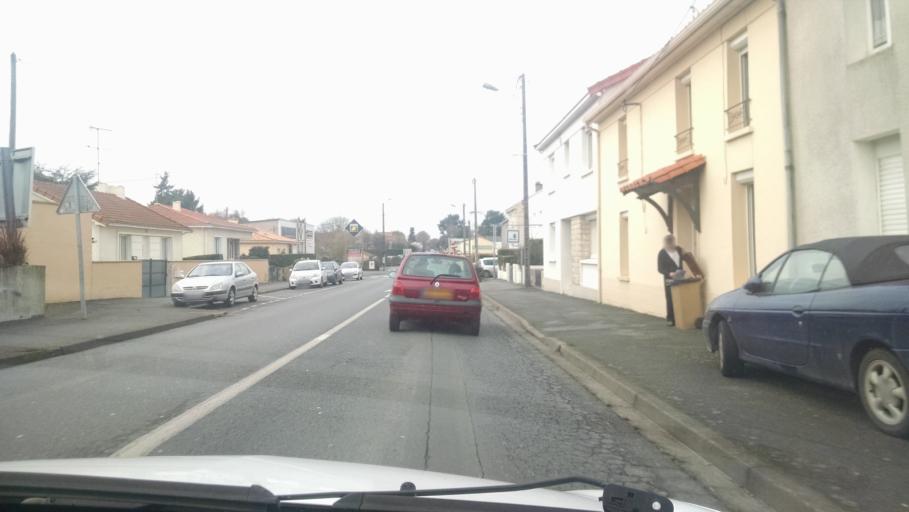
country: FR
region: Pays de la Loire
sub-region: Departement de Maine-et-Loire
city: La Seguiniere
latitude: 47.0602
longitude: -0.9350
